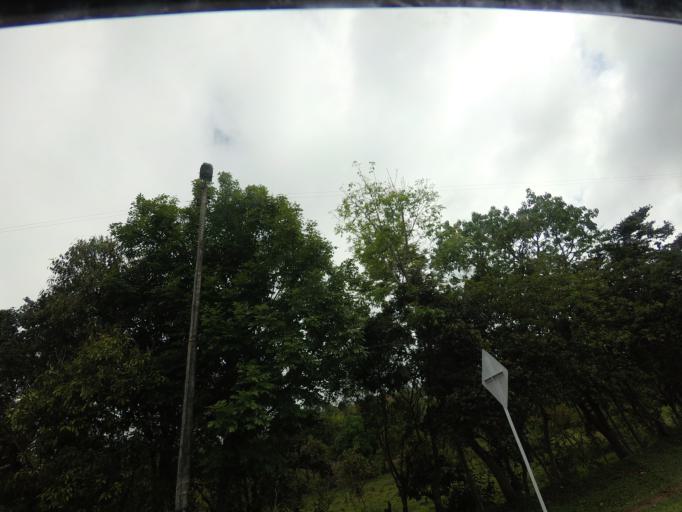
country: CO
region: Huila
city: San Agustin
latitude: 1.8862
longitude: -76.2768
